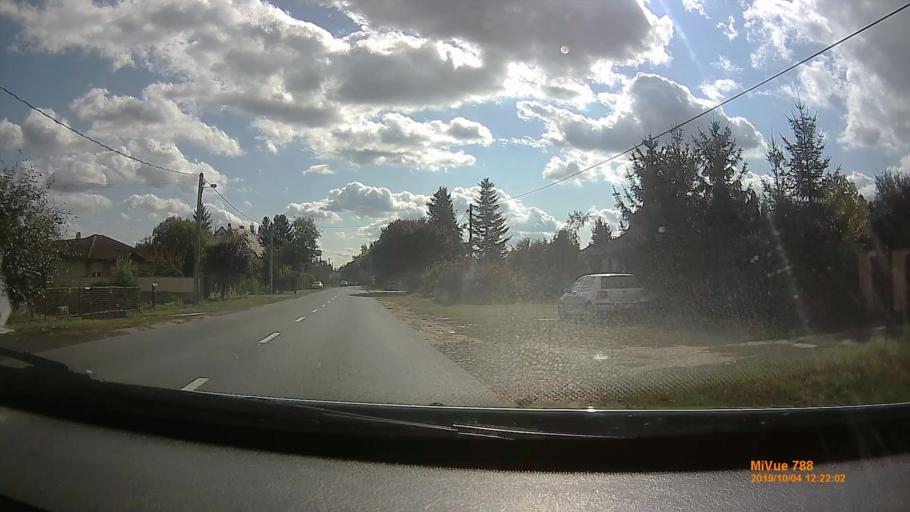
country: HU
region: Szabolcs-Szatmar-Bereg
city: Kotaj
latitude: 48.0156
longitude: 21.6871
